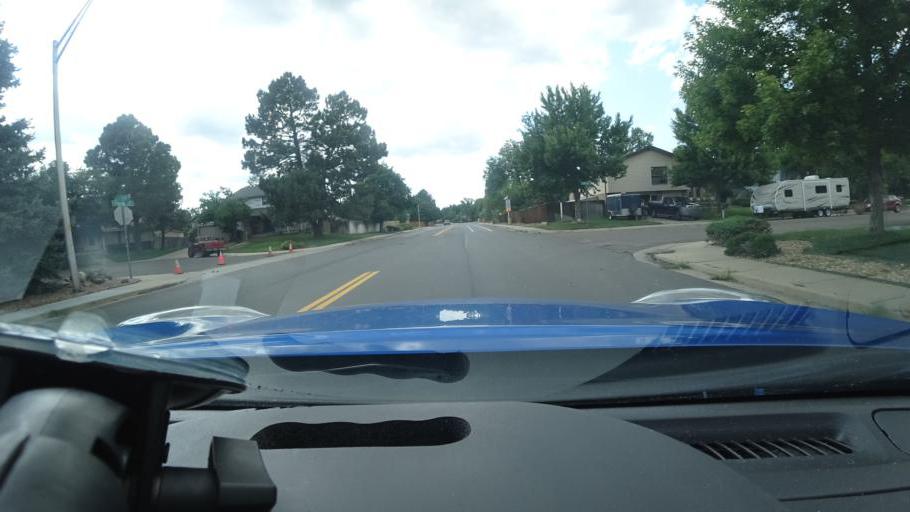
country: US
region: Colorado
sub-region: Adams County
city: Aurora
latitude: 39.6888
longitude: -104.8548
